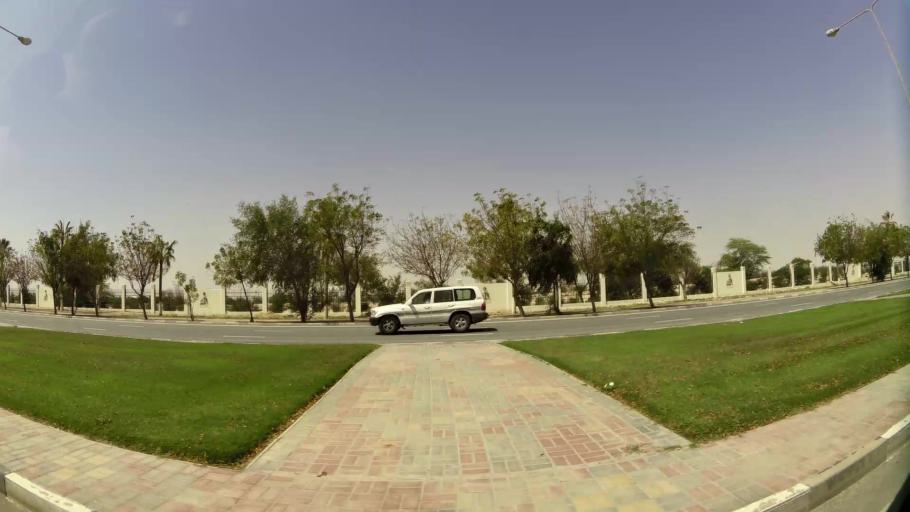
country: QA
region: Baladiyat ad Dawhah
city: Doha
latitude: 25.3613
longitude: 51.4952
